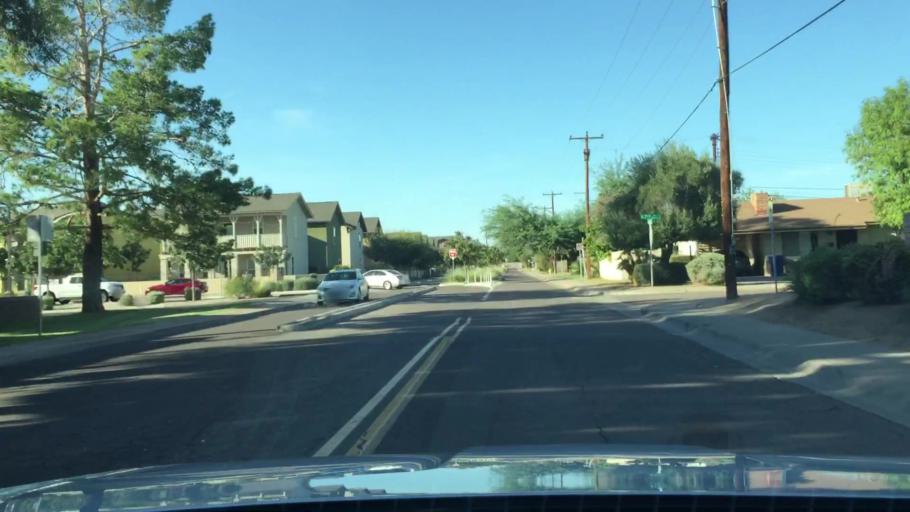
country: US
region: Arizona
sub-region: Maricopa County
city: Tempe Junction
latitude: 33.4225
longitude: -111.9652
